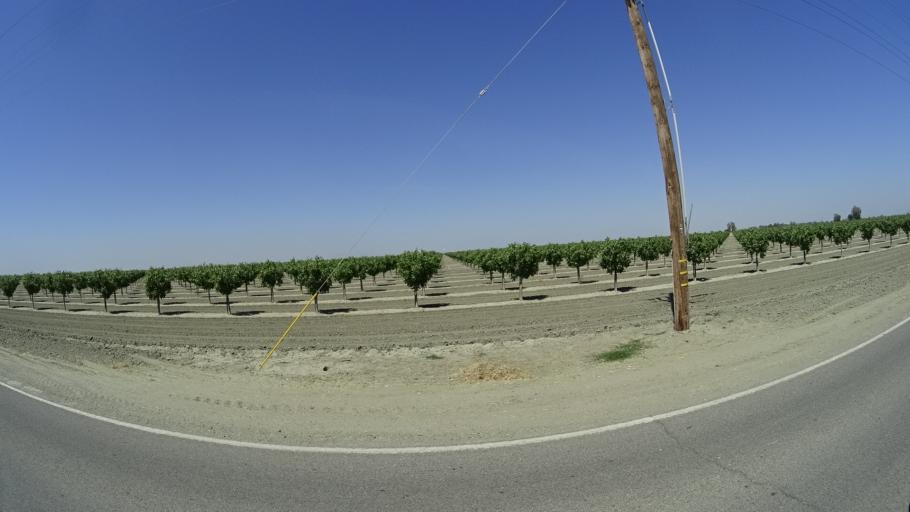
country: US
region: California
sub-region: Kings County
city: Corcoran
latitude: 36.0779
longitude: -119.5720
